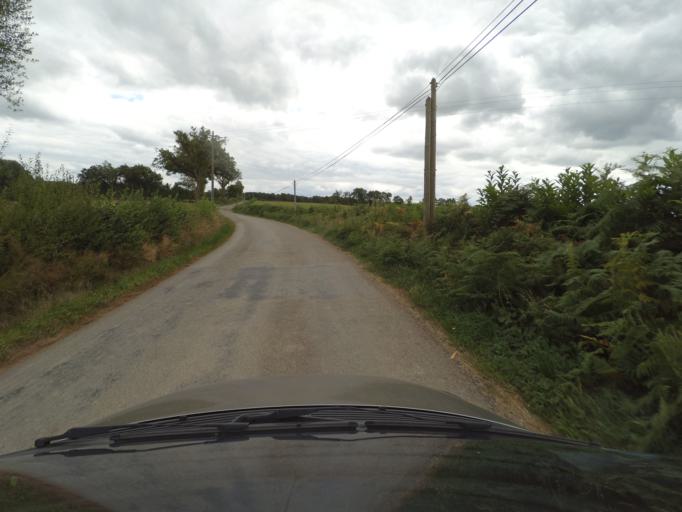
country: FR
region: Limousin
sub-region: Departement de la Haute-Vienne
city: Arnac-la-Poste
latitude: 46.2791
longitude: 1.2611
